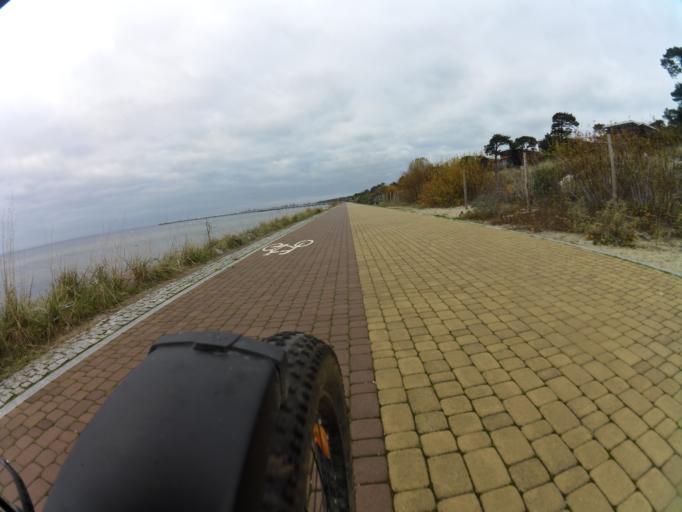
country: PL
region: Pomeranian Voivodeship
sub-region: Powiat pucki
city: Jastarnia
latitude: 54.6785
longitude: 18.7154
